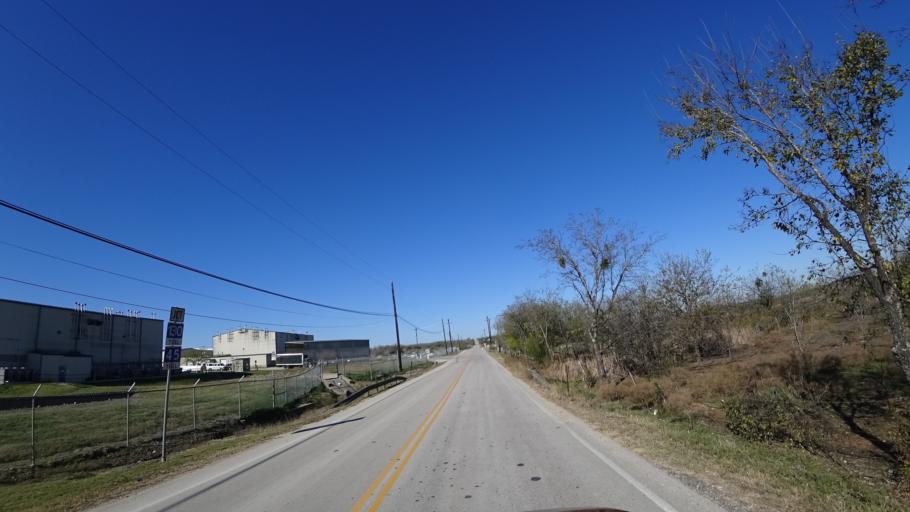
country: US
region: Texas
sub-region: Travis County
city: Onion Creek
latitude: 30.1201
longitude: -97.6642
